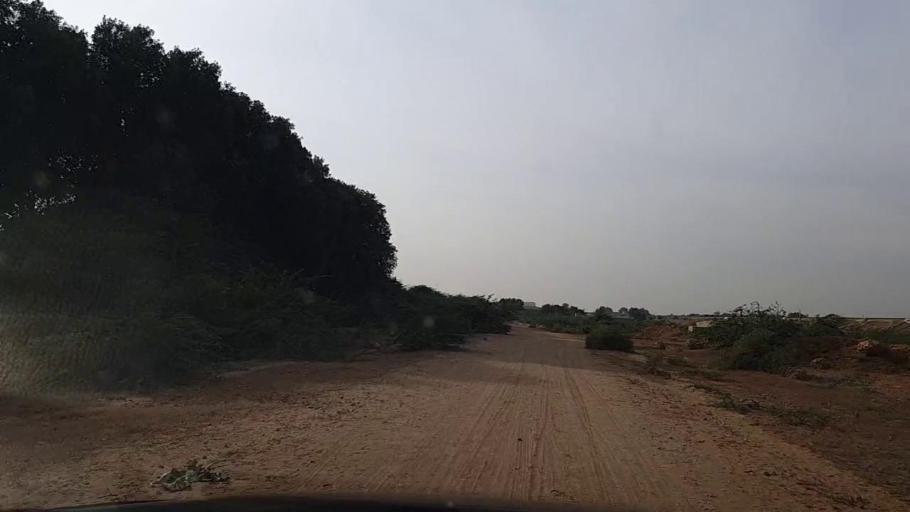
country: PK
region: Sindh
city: Gharo
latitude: 24.7952
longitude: 67.5376
